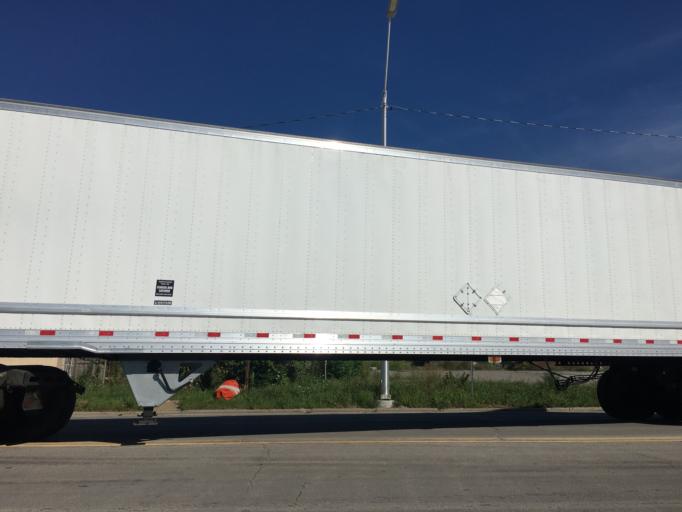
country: US
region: Michigan
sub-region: Wayne County
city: Detroit
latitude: 42.3119
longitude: -83.0909
